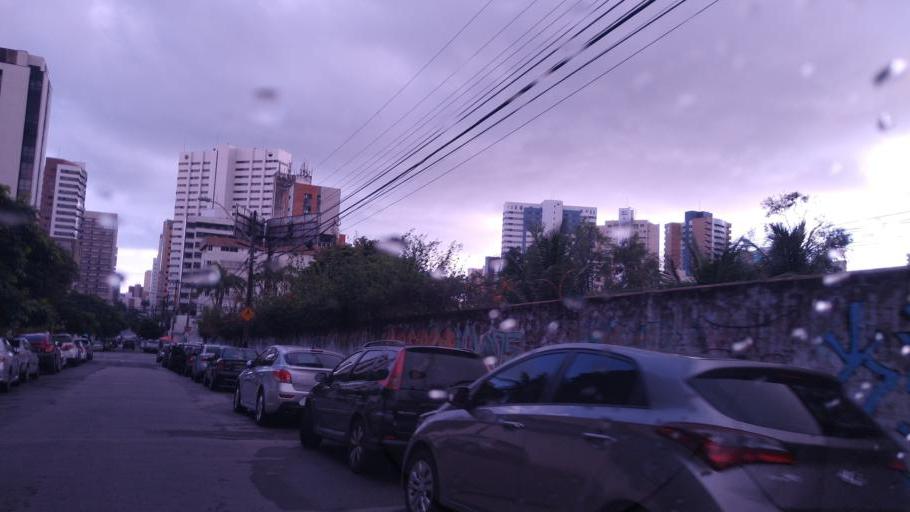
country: BR
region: Ceara
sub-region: Fortaleza
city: Fortaleza
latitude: -3.7382
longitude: -38.4947
